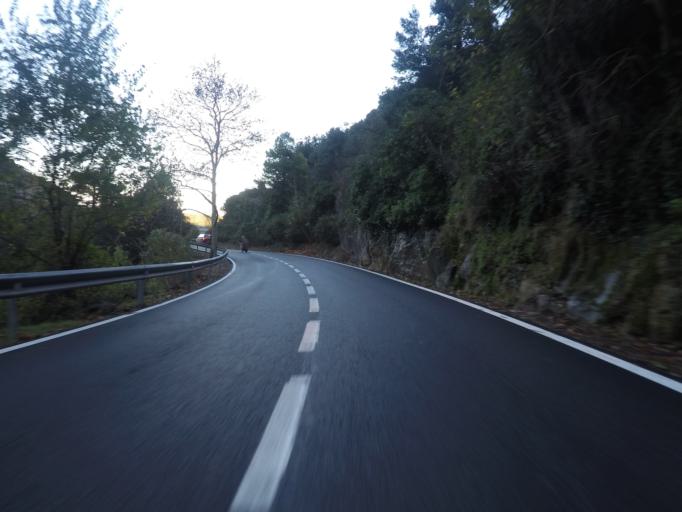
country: ES
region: Catalonia
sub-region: Provincia de Barcelona
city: Monistrol de Montserrat
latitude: 41.6105
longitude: 1.8241
